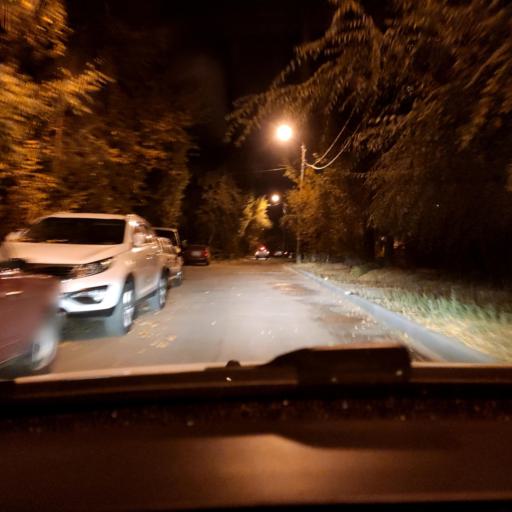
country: RU
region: Voronezj
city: Voronezh
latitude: 51.6485
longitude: 39.1405
